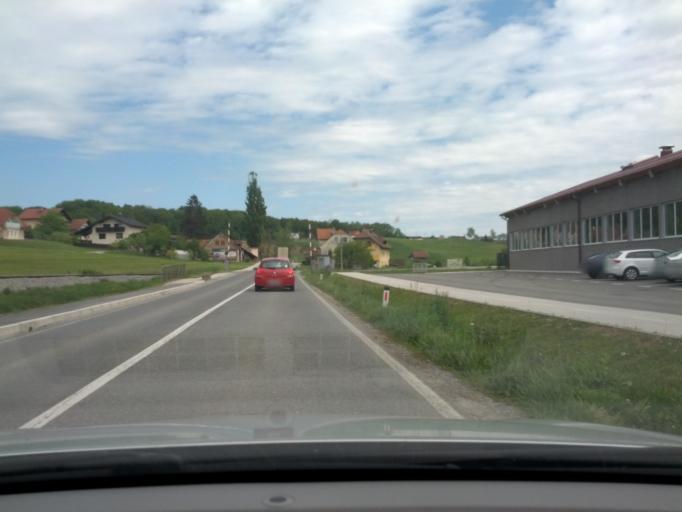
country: SI
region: Smarje pri Jelsah
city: Smarje pri Jelsah
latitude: 46.2328
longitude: 15.5310
